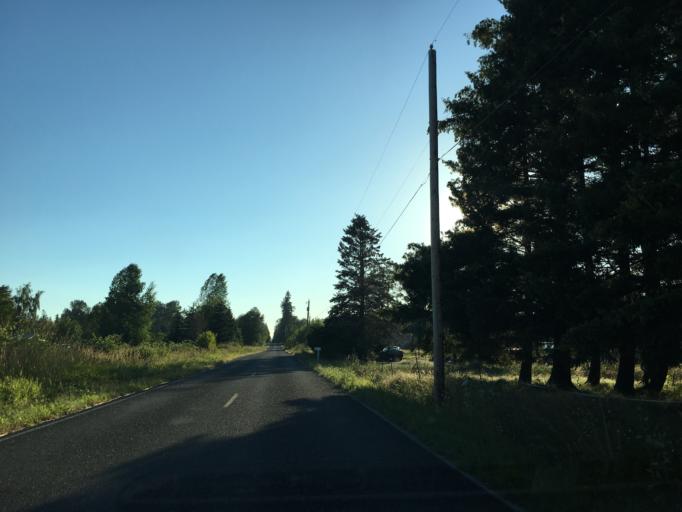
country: US
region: Washington
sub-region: Whatcom County
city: Geneva
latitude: 48.8181
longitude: -122.3475
